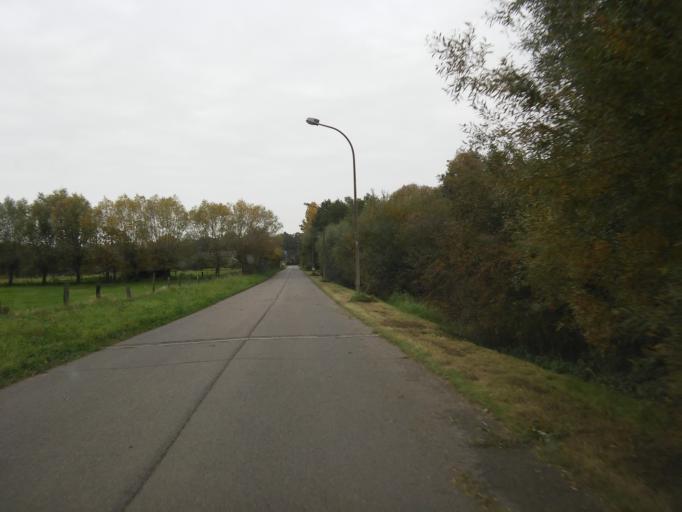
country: BE
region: Flanders
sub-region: Provincie Antwerpen
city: Willebroek
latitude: 51.0616
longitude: 4.3813
